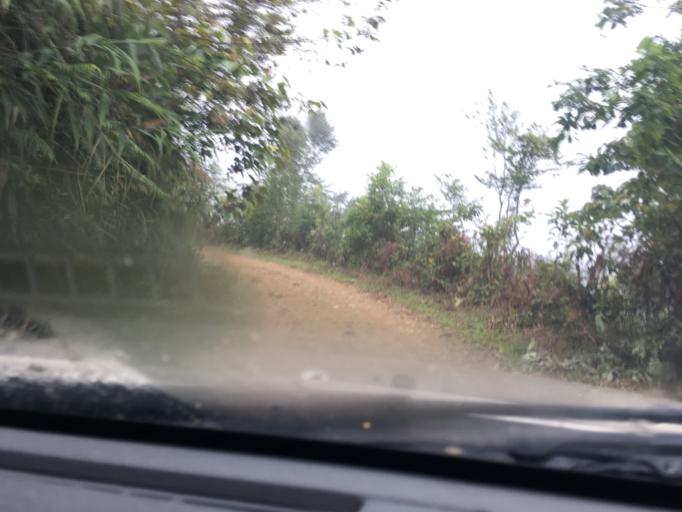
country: LA
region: Phongsali
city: Phongsali
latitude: 21.4276
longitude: 102.2638
